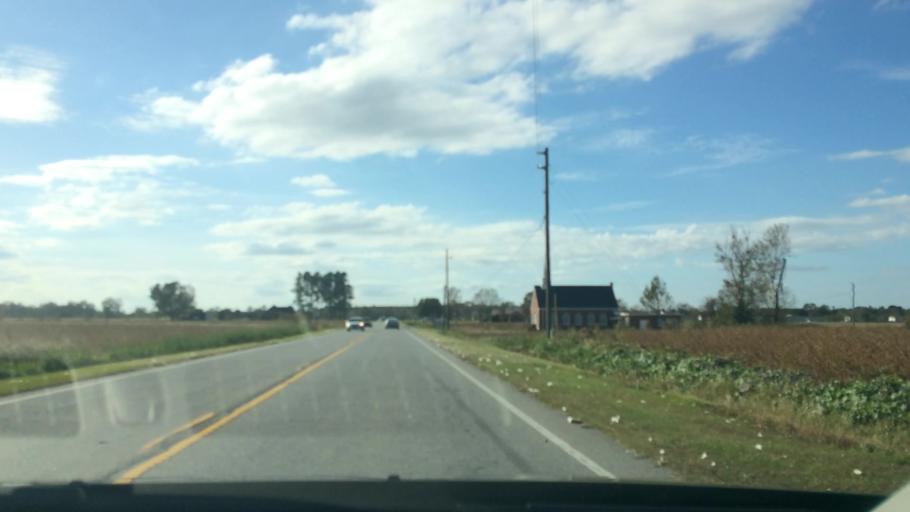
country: US
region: North Carolina
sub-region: Greene County
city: Snow Hill
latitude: 35.4392
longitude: -77.8045
